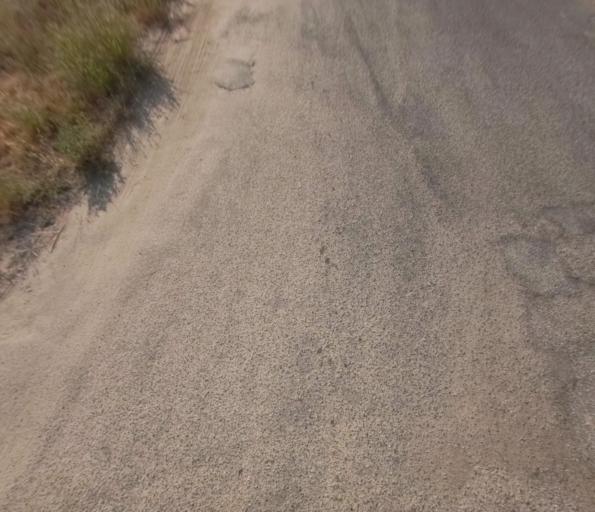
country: US
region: California
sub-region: Madera County
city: Yosemite Lakes
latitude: 37.2161
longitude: -119.9068
